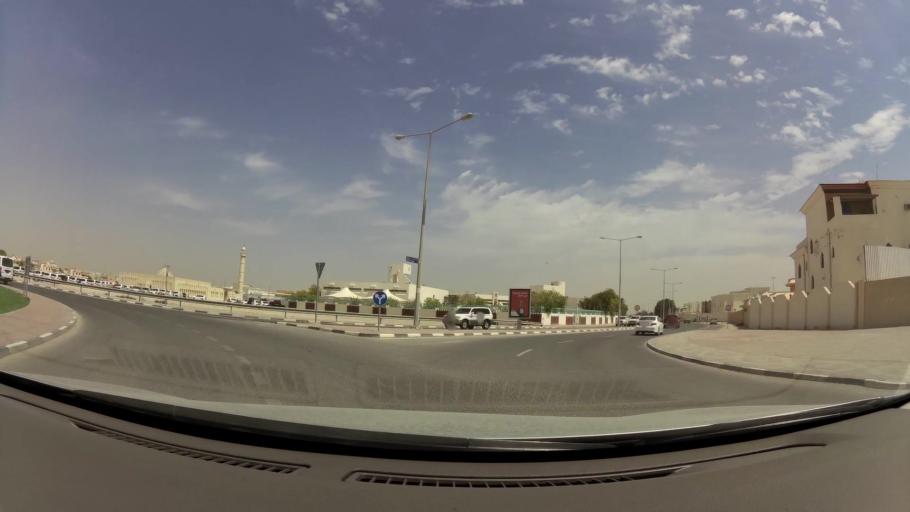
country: QA
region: Baladiyat ar Rayyan
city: Ar Rayyan
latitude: 25.2839
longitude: 51.4078
